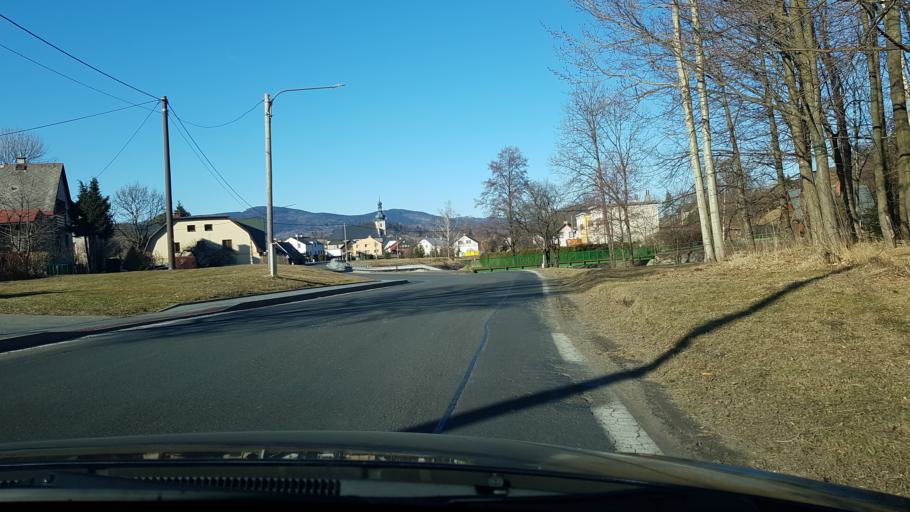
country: CZ
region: Olomoucky
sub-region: Okres Jesenik
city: Jesenik
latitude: 50.1875
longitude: 17.1953
